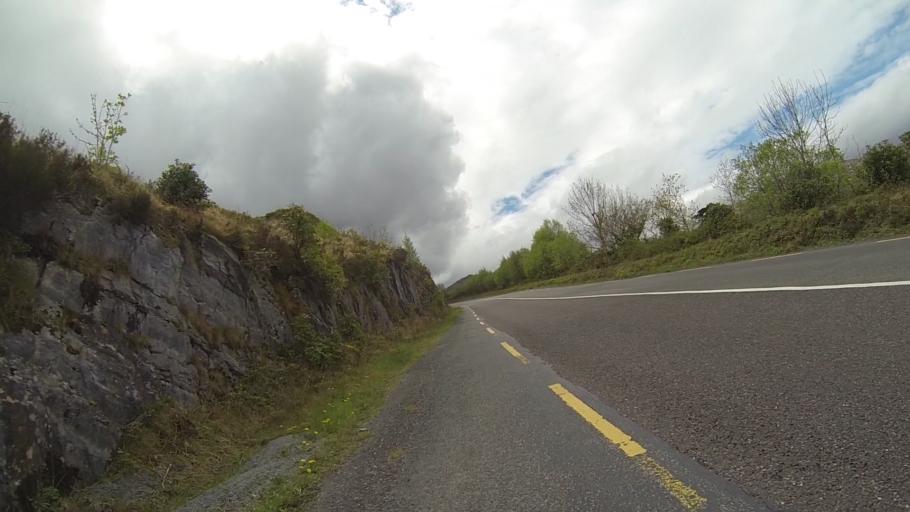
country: IE
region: Munster
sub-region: County Cork
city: Bantry
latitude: 51.7272
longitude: -9.5718
